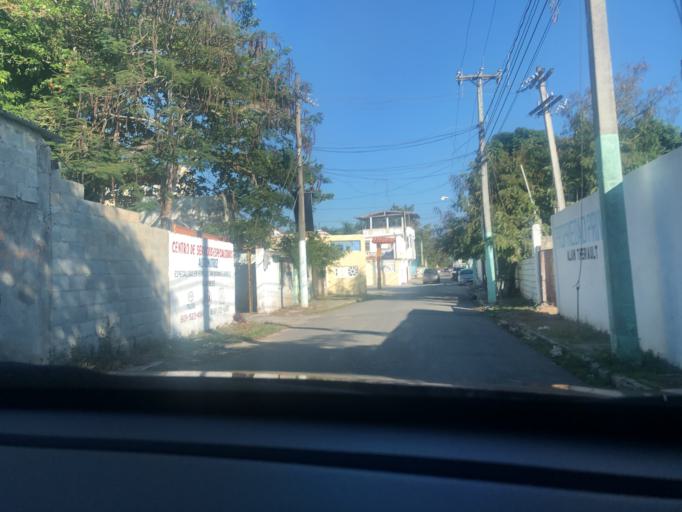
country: DO
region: Santo Domingo
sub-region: Santo Domingo
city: Boca Chica
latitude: 18.4540
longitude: -69.6106
